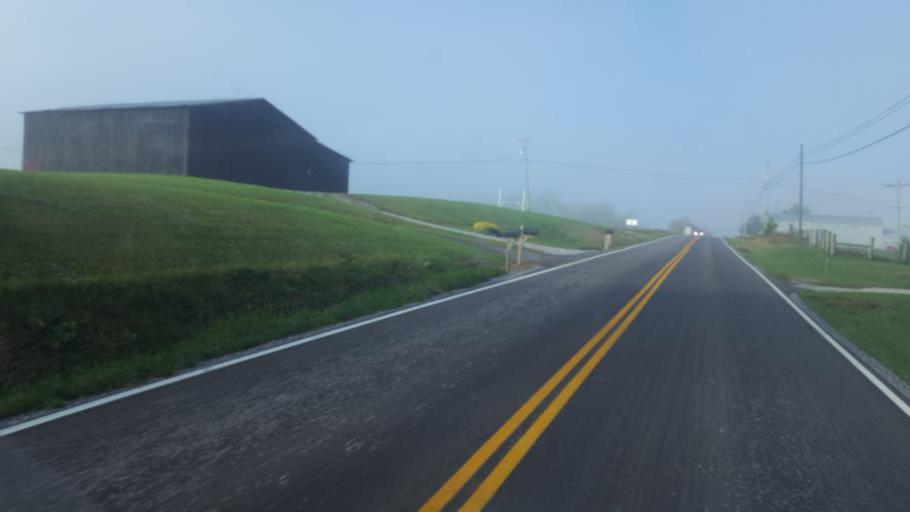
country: US
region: Kentucky
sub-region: Fleming County
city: Flemingsburg
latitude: 38.4826
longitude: -83.6417
